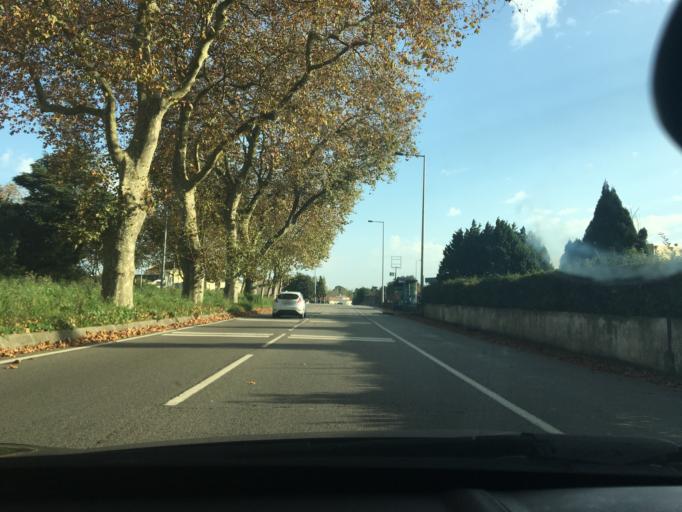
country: PT
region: Porto
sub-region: Matosinhos
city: Senhora da Hora
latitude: 41.1776
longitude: -8.6628
